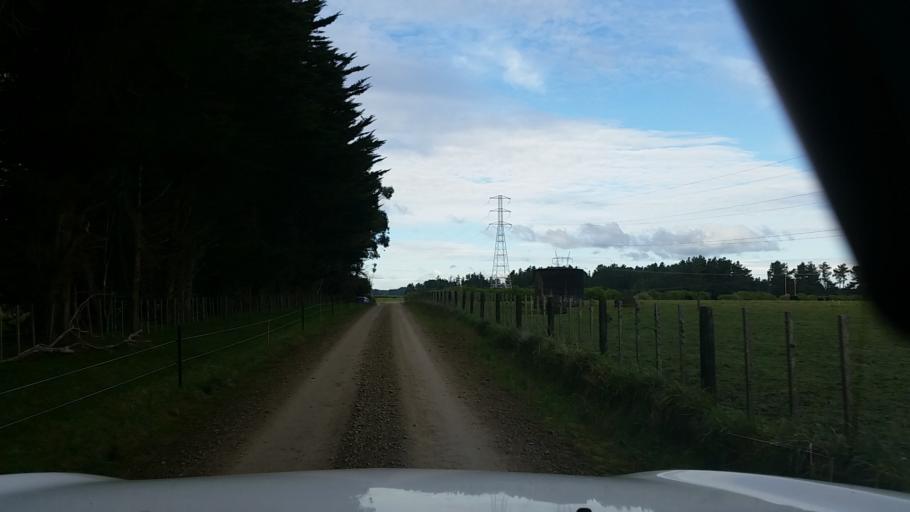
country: NZ
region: Taranaki
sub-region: South Taranaki District
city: Patea
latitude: -39.7882
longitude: 174.7447
